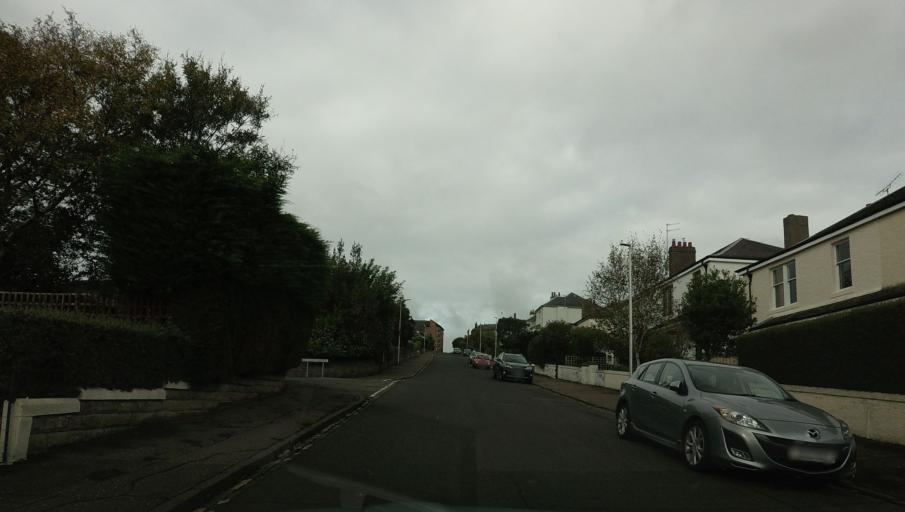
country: GB
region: Scotland
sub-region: Dundee City
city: Dundee
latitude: 56.4584
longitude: -3.0017
